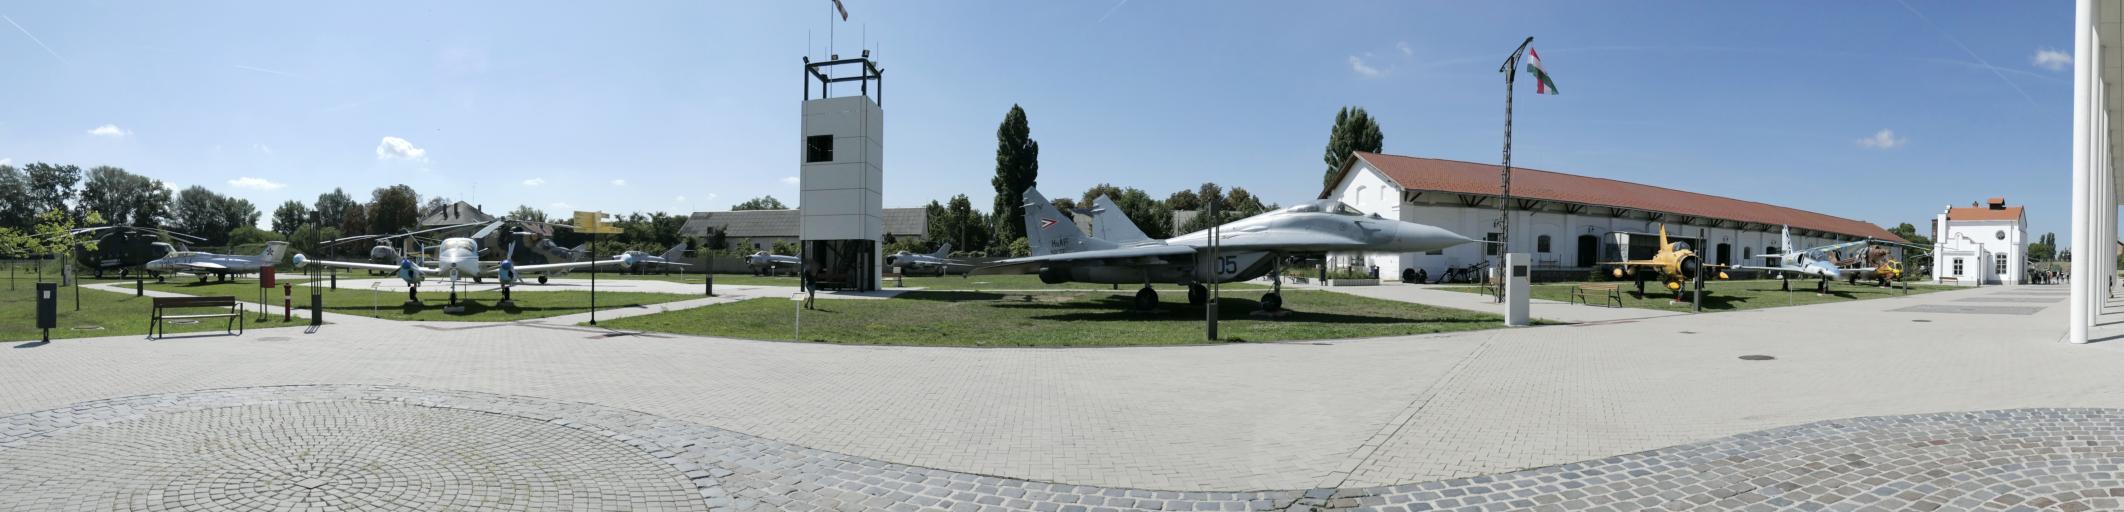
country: HU
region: Jasz-Nagykun-Szolnok
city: Szolnok
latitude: 47.1672
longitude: 20.1801
